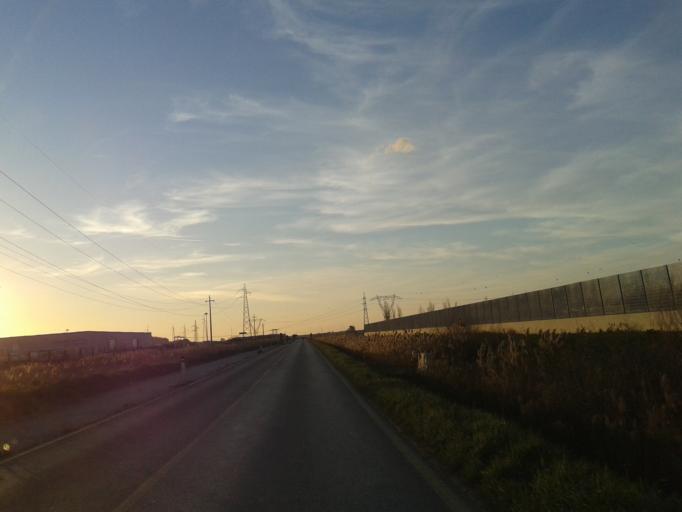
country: IT
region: Tuscany
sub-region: Provincia di Livorno
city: Guasticce
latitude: 43.5971
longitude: 10.3983
